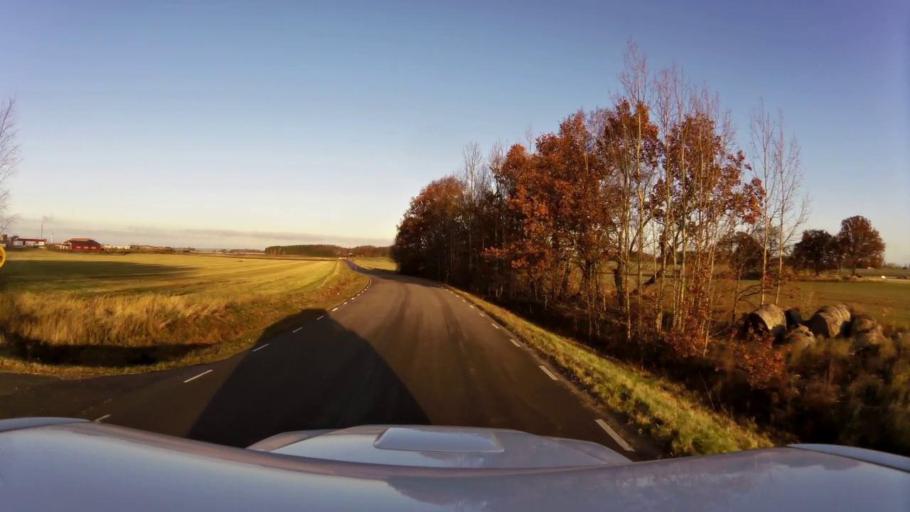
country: SE
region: OEstergoetland
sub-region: Linkopings Kommun
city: Ekangen
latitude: 58.4365
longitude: 15.6804
